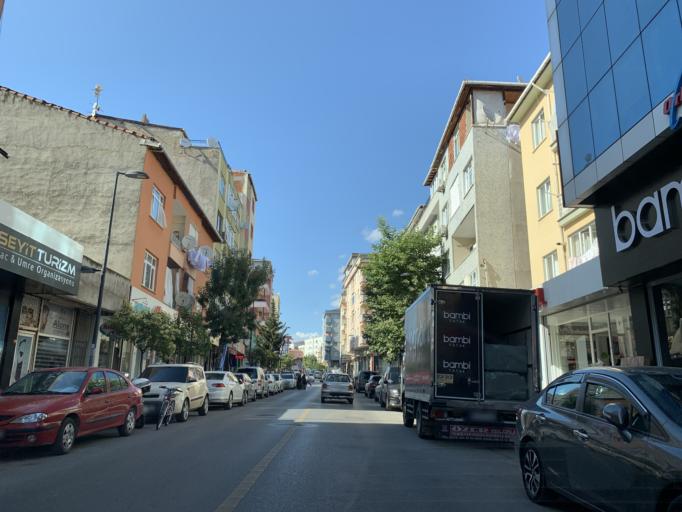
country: TR
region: Istanbul
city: Pendik
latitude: 40.8763
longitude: 29.2700
